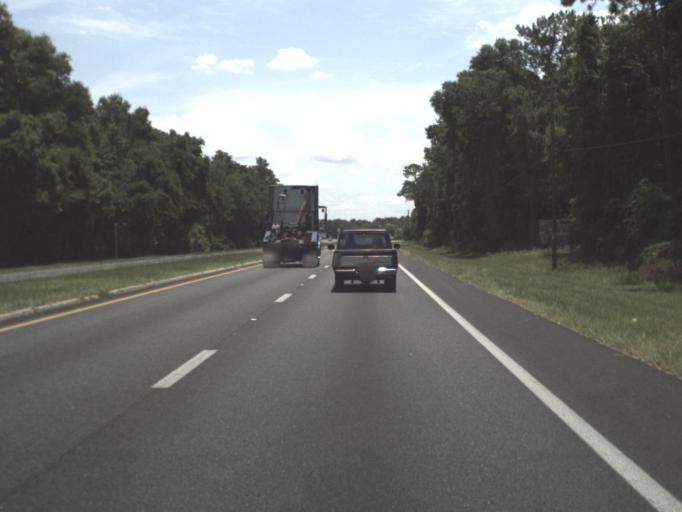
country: US
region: Florida
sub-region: Levy County
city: Manatee Road
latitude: 29.5891
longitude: -82.9611
